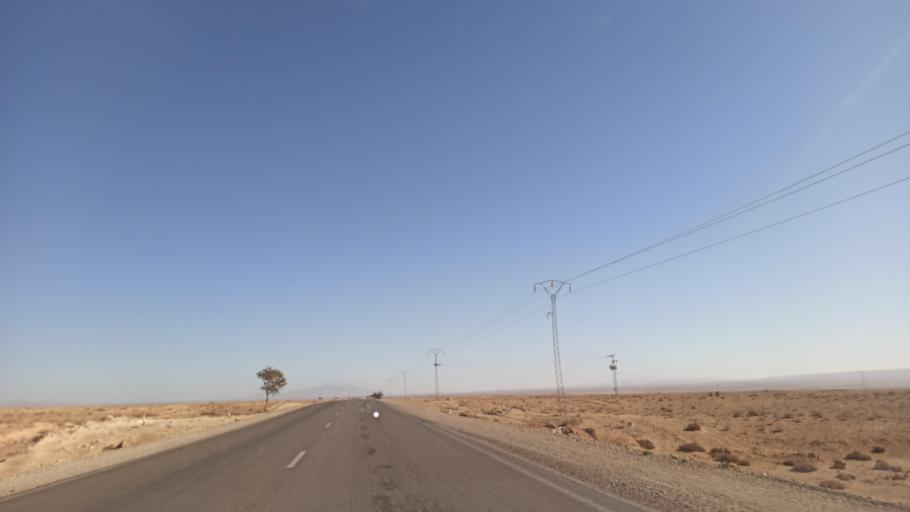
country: TN
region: Gafsa
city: Al Metlaoui
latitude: 34.3128
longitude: 8.4838
